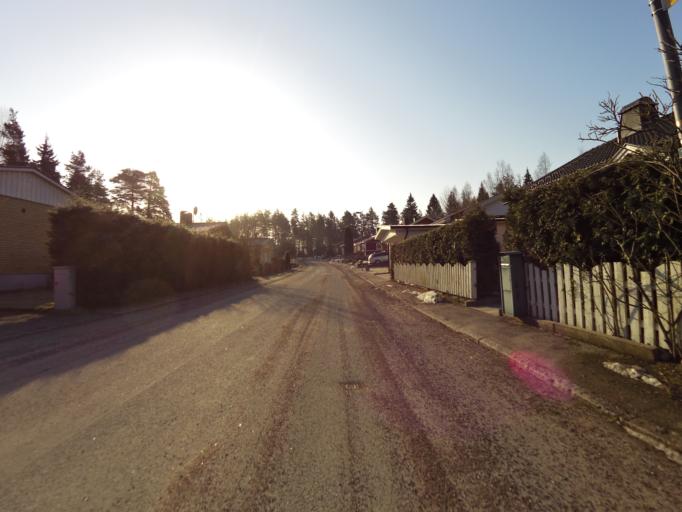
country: SE
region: Gaevleborg
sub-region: Gavle Kommun
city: Gavle
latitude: 60.6576
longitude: 17.1209
